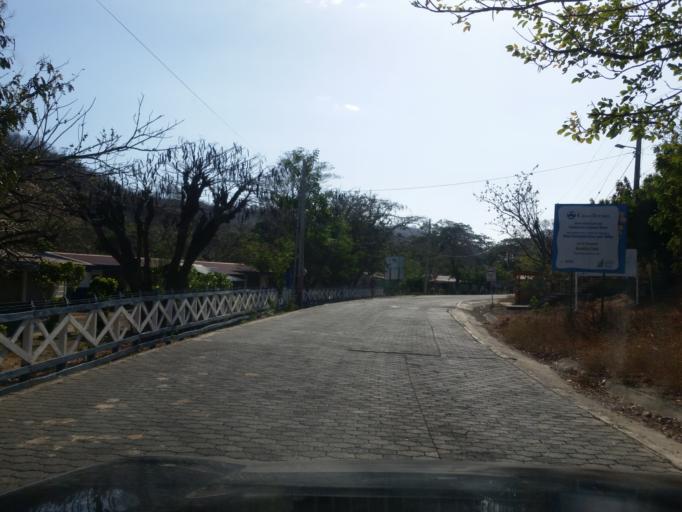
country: NI
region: Rivas
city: Tola
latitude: 11.3932
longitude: -85.9687
